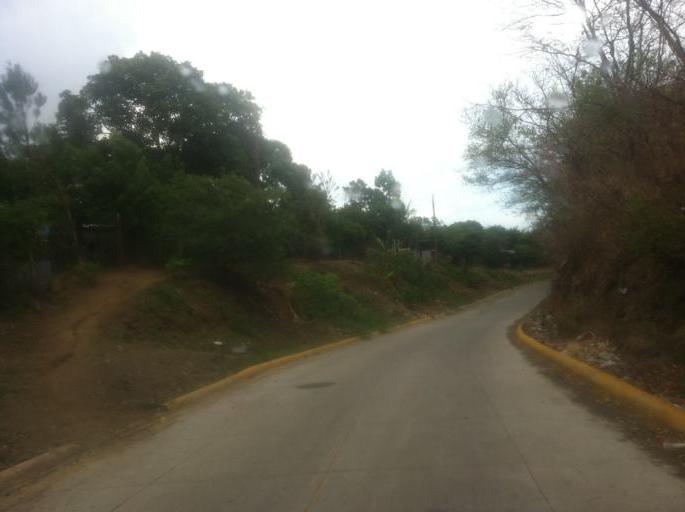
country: NI
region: Managua
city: Managua
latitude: 12.1055
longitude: -86.2388
